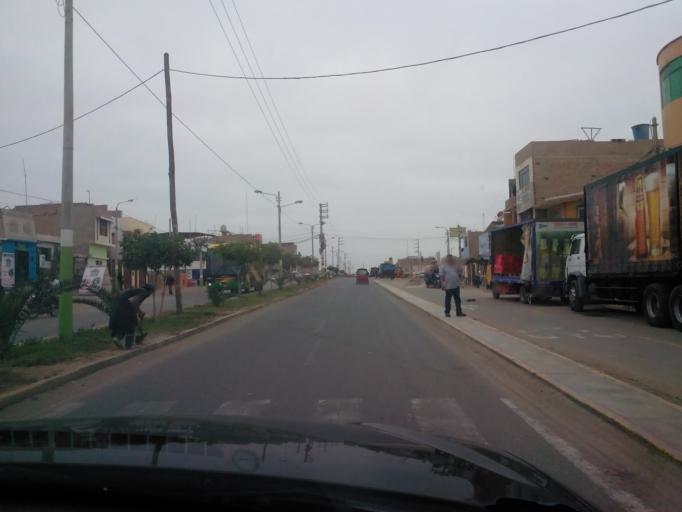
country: PE
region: Ica
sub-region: Provincia de Pisco
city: San Clemente
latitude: -13.6822
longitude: -76.1567
